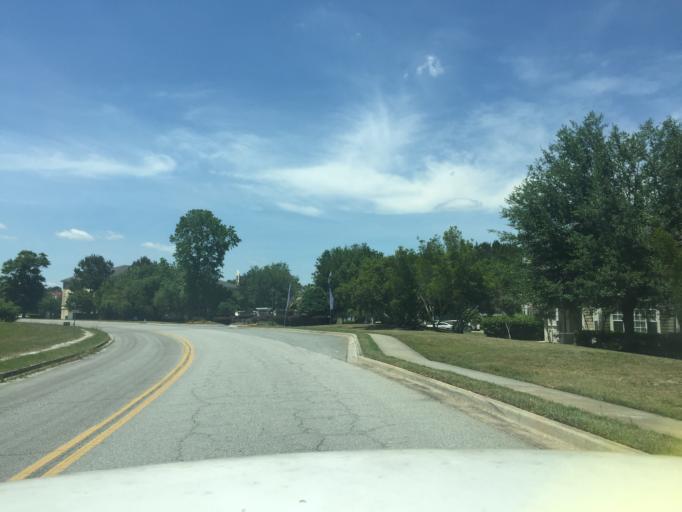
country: US
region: Georgia
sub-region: Chatham County
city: Georgetown
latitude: 32.0065
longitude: -81.2747
